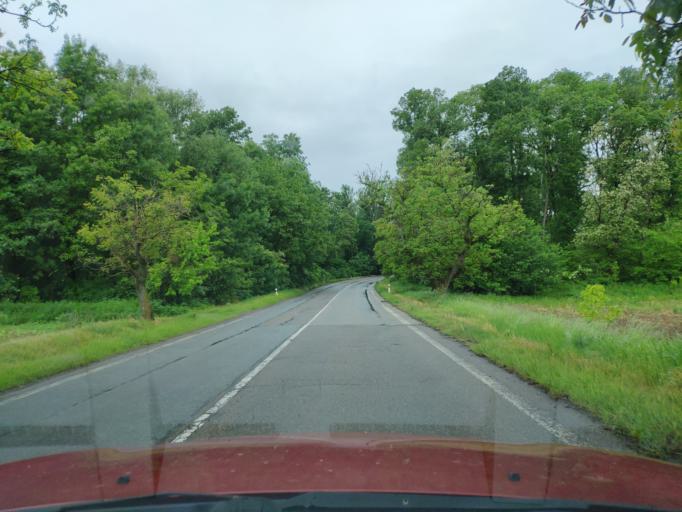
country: HU
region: Borsod-Abauj-Zemplen
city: Ricse
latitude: 48.4349
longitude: 21.9561
